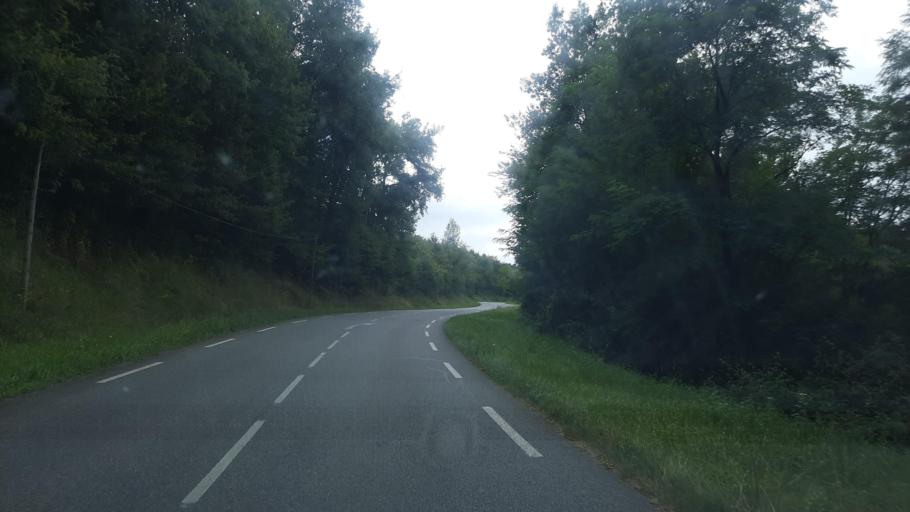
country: FR
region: Midi-Pyrenees
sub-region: Departement des Hautes-Pyrenees
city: Trie-sur-Baise
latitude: 43.3119
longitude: 0.3798
